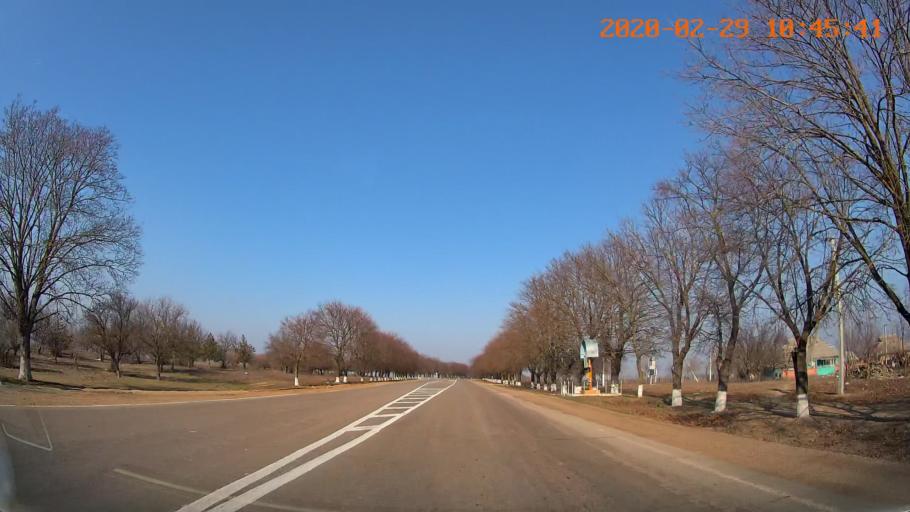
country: MD
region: Telenesti
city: Grigoriopol
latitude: 47.0778
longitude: 29.3805
